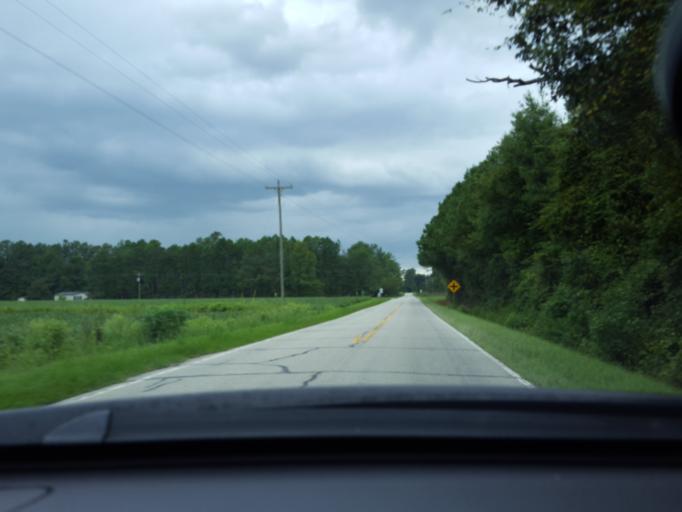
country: US
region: North Carolina
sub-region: Duplin County
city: Rose Hill
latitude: 34.8005
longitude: -78.2350
